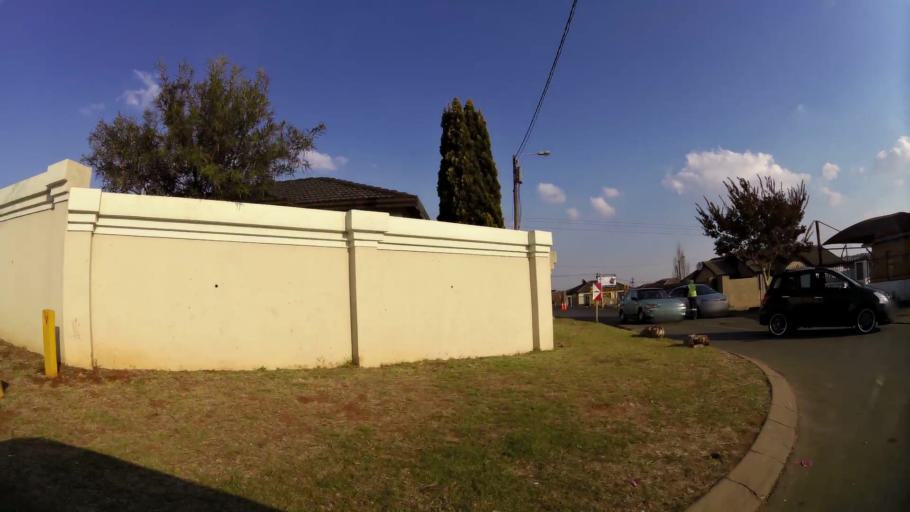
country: ZA
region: Gauteng
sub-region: Ekurhuleni Metropolitan Municipality
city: Tembisa
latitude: -25.9515
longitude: 28.2095
